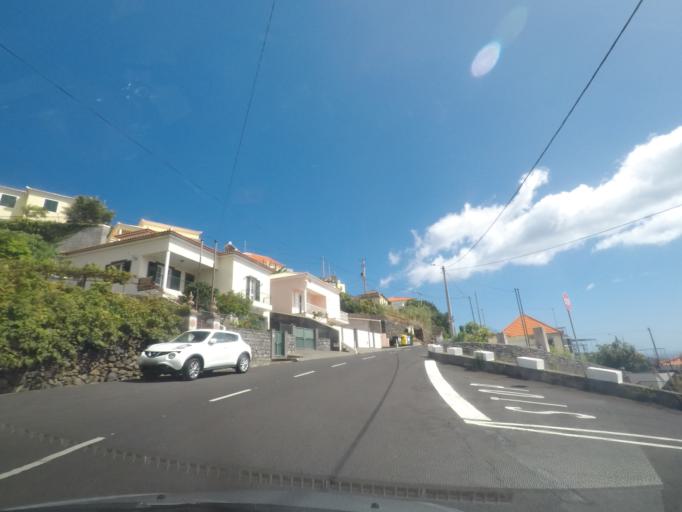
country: PT
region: Madeira
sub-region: Ribeira Brava
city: Campanario
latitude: 32.6675
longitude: -17.0509
